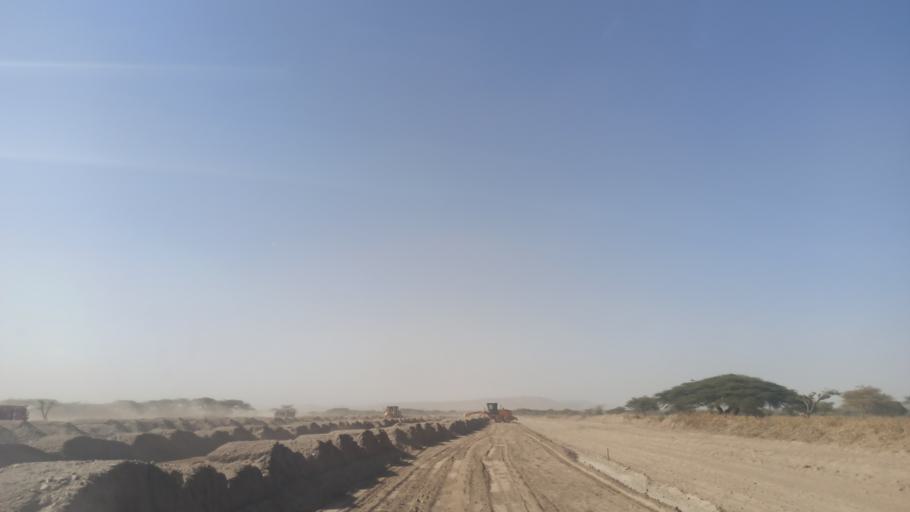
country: ET
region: Oromiya
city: Ziway
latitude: 7.7417
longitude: 38.6196
